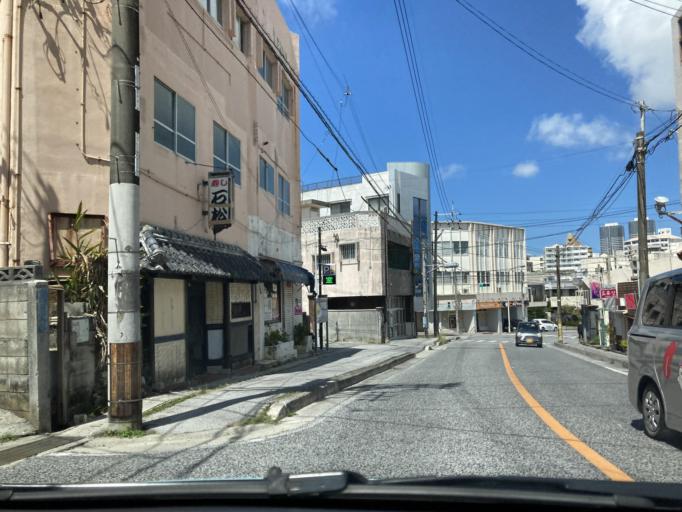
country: JP
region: Okinawa
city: Naha-shi
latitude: 26.2120
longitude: 127.6961
